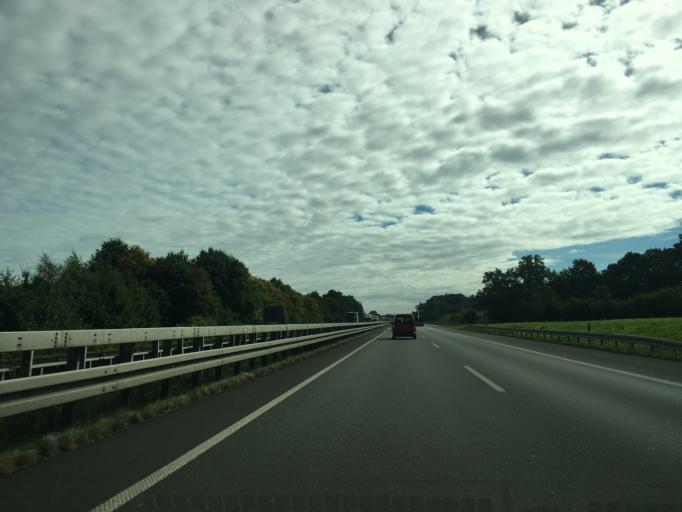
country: DE
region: Lower Saxony
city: Neuenkirchen
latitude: 52.1976
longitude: 8.4124
